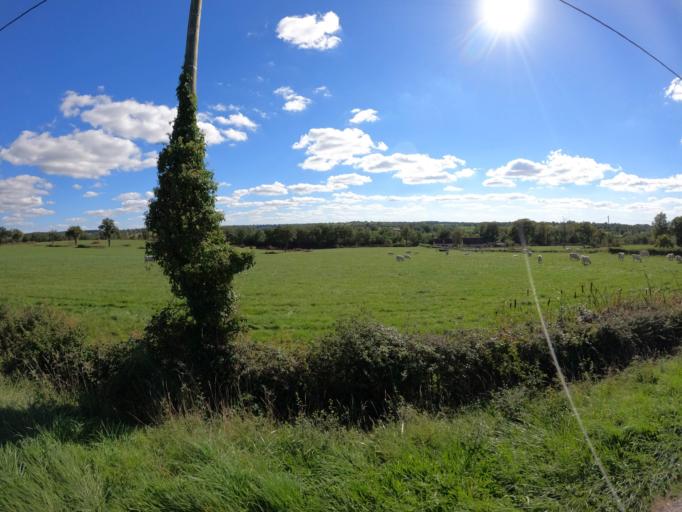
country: FR
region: Auvergne
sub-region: Departement de l'Allier
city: Doyet
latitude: 46.3975
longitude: 2.8818
